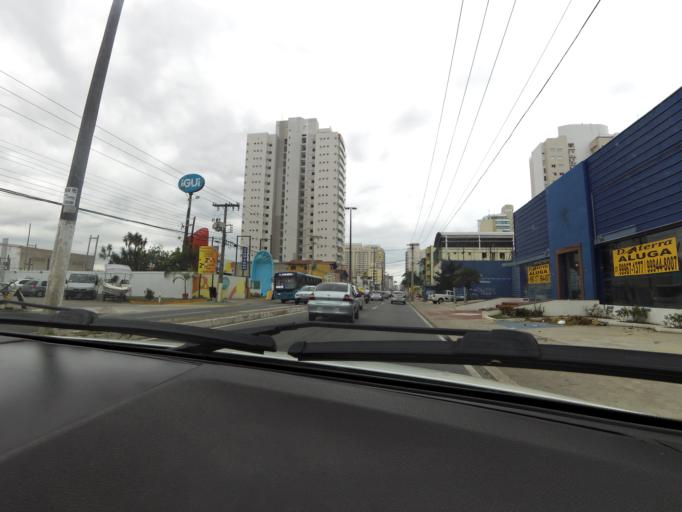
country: BR
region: Espirito Santo
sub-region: Vila Velha
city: Vila Velha
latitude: -20.3760
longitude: -40.3067
